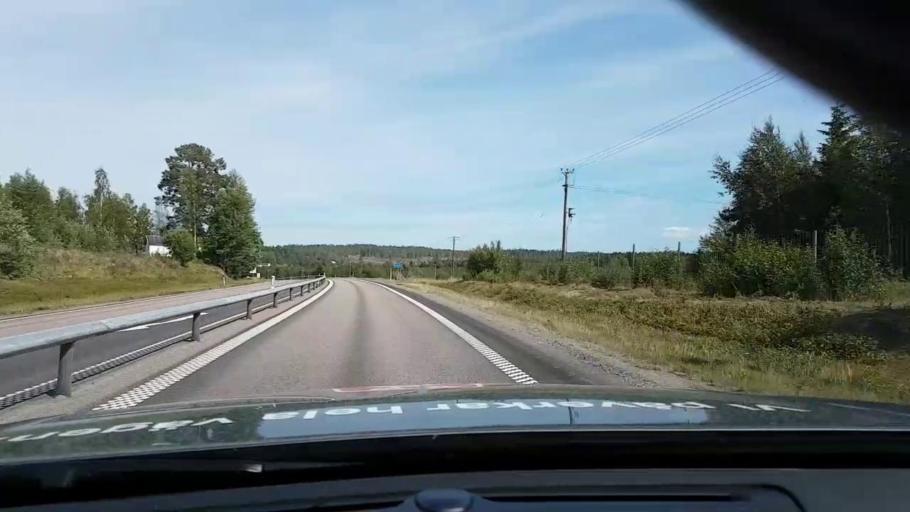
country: SE
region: Vaesternorrland
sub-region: OErnskoeldsviks Kommun
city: Husum
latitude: 63.3240
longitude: 19.0474
